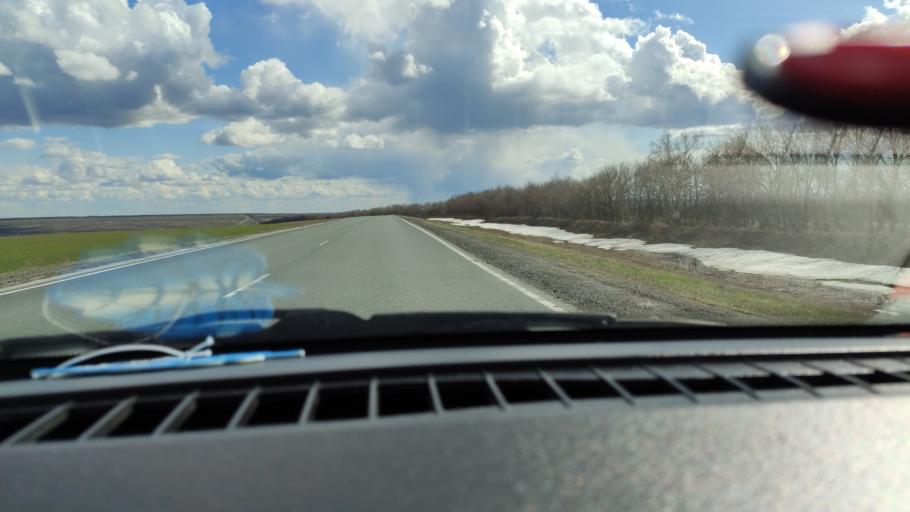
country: RU
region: Saratov
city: Dukhovnitskoye
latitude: 52.7657
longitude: 48.2379
